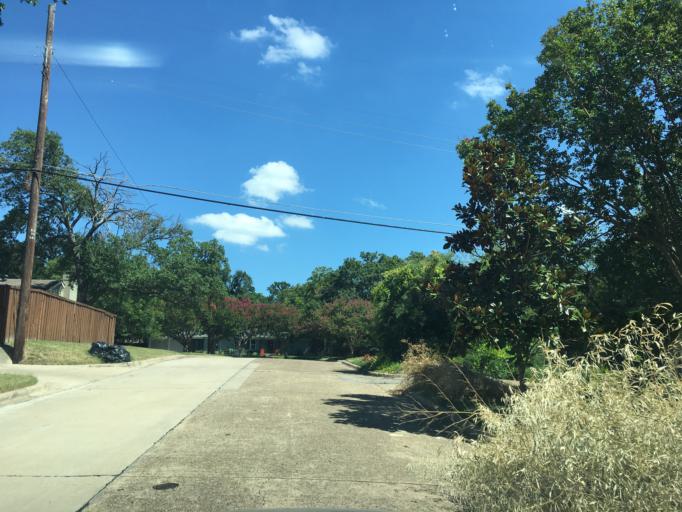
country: US
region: Texas
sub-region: Dallas County
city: Highland Park
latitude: 32.8408
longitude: -96.7020
